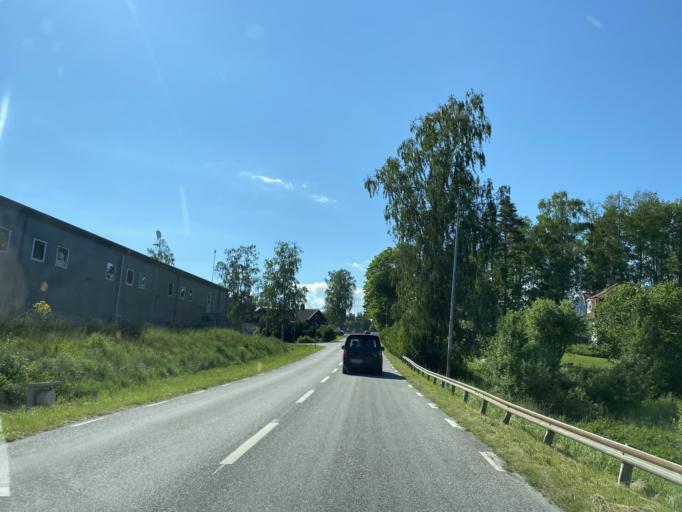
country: SE
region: Stockholm
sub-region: Norrtalje Kommun
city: Norrtalje
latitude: 59.7699
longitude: 18.6849
